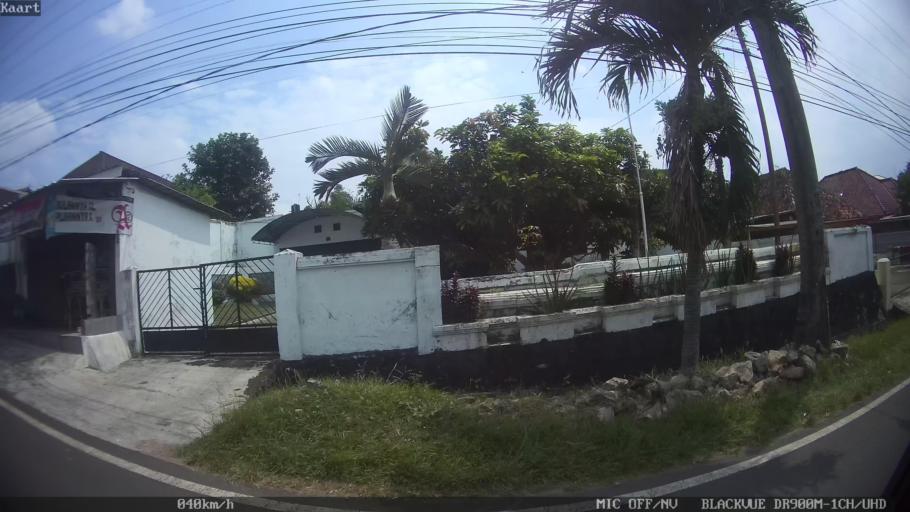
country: ID
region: Lampung
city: Bandarlampung
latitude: -5.4400
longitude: 105.2640
